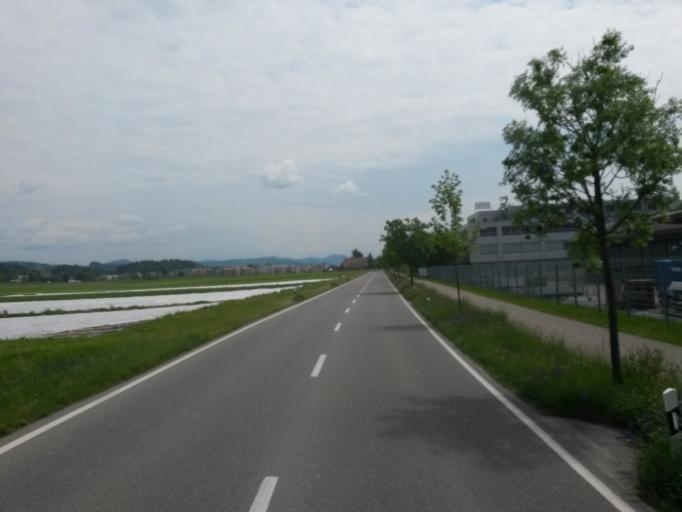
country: CH
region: Zurich
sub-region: Bezirk Pfaeffikon
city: Fehraltorf
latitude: 47.3954
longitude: 8.7399
